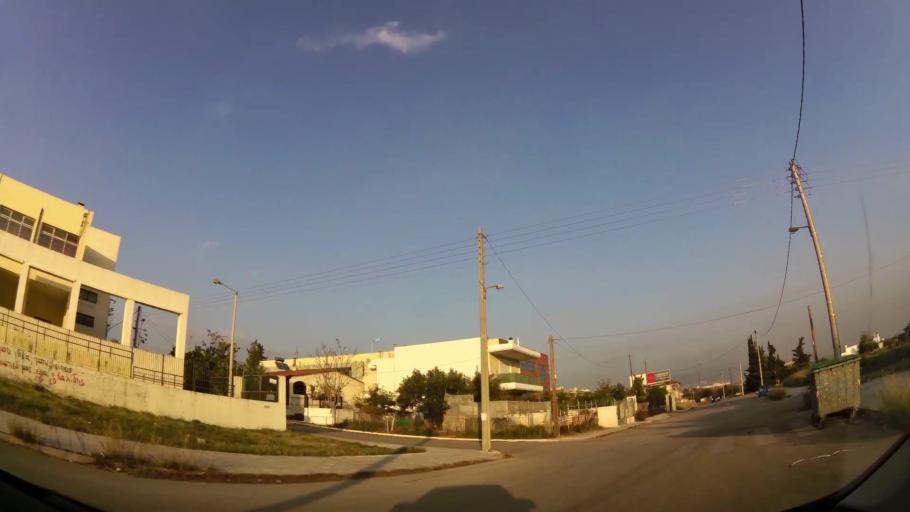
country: GR
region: Attica
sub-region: Nomarchia Anatolikis Attikis
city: Acharnes
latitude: 38.0989
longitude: 23.7421
